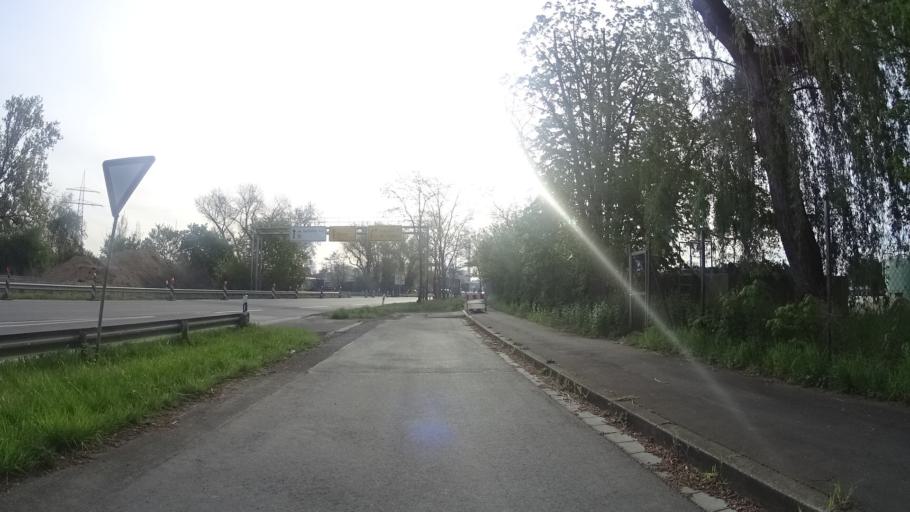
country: DE
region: Rheinland-Pfalz
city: Budenheim
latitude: 50.0291
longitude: 8.2173
